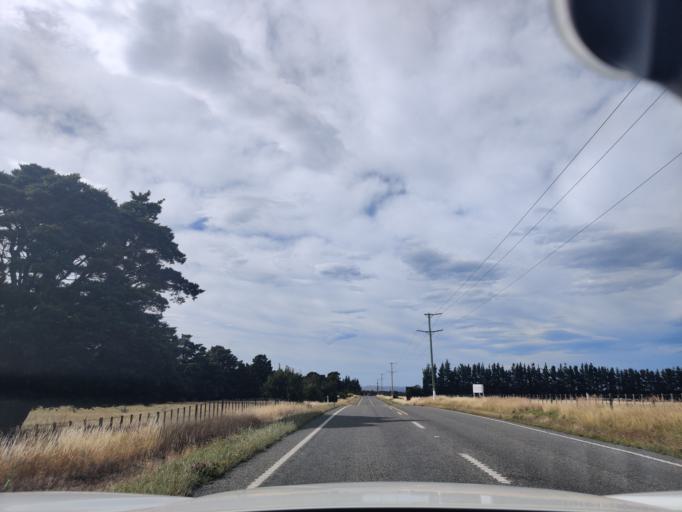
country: NZ
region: Wellington
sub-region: Masterton District
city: Masterton
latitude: -40.8367
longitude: 175.6294
